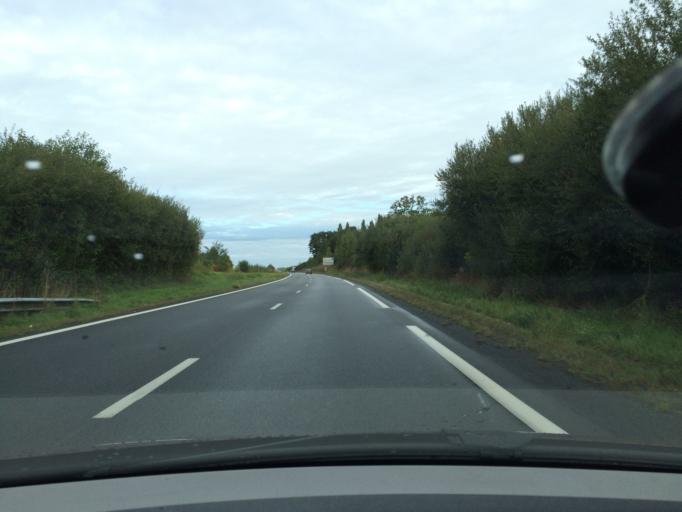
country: FR
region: Brittany
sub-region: Departement d'Ille-et-Vilaine
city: Janze
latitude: 47.9671
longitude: -1.5294
